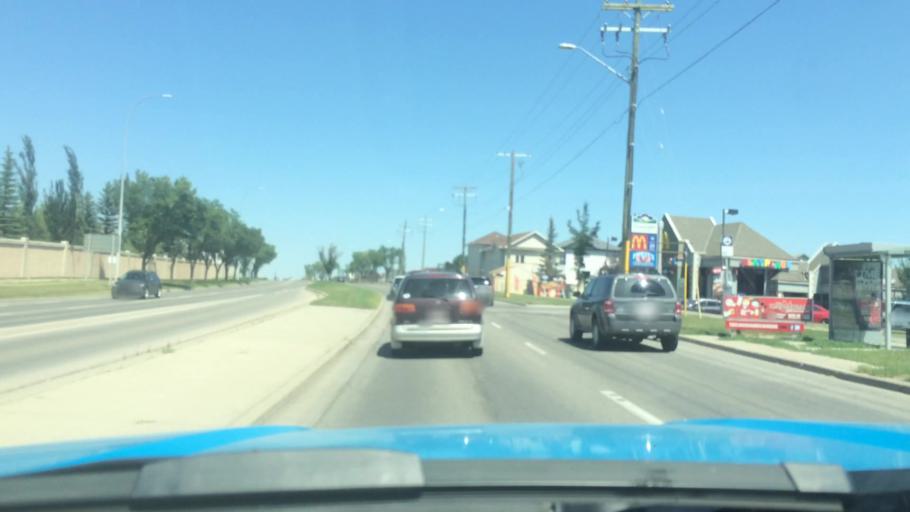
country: CA
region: Alberta
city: Calgary
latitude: 51.1487
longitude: -114.0731
